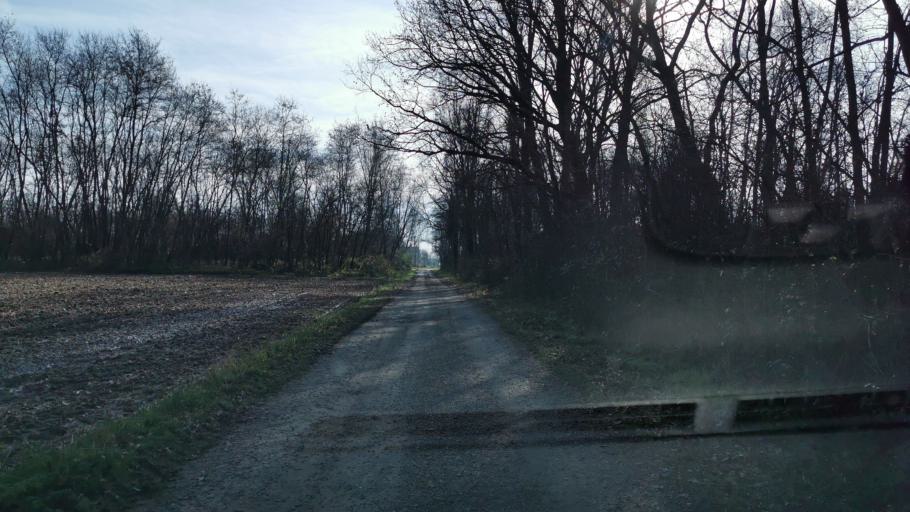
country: IT
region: Piedmont
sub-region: Provincia di Torino
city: Bosconero
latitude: 45.2730
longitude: 7.7758
